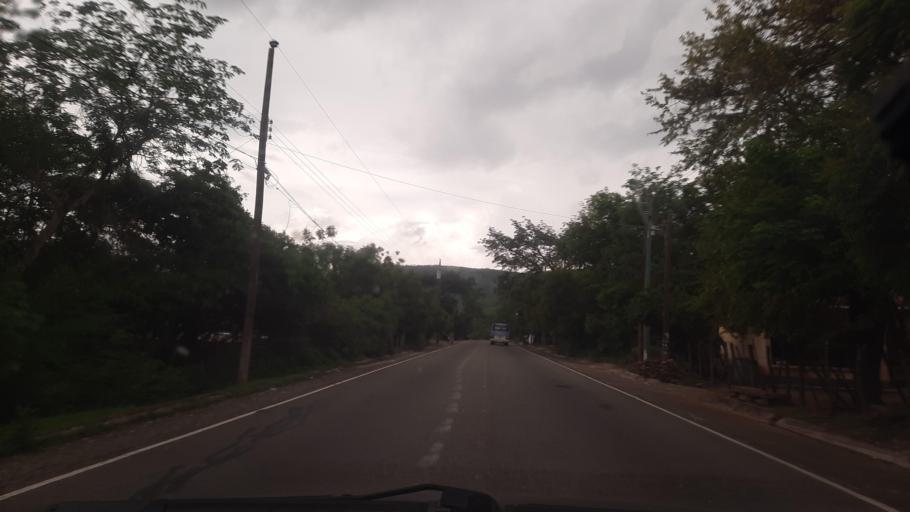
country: GT
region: Zacapa
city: San Jorge
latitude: 14.9136
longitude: -89.5296
